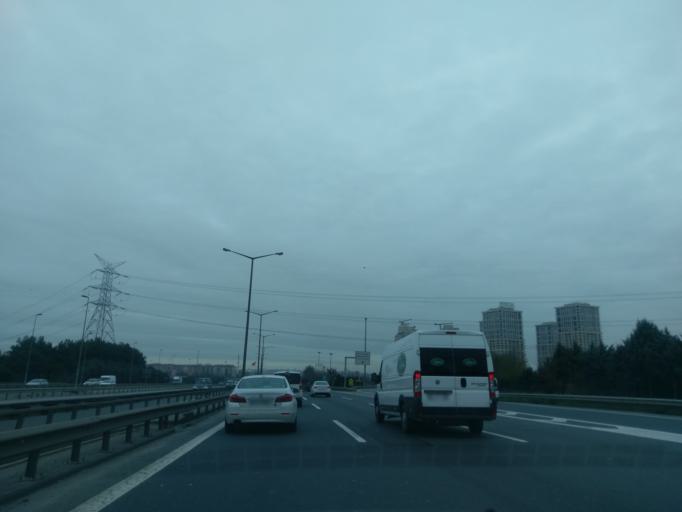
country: TR
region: Istanbul
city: Sultangazi
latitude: 41.0759
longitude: 28.8707
